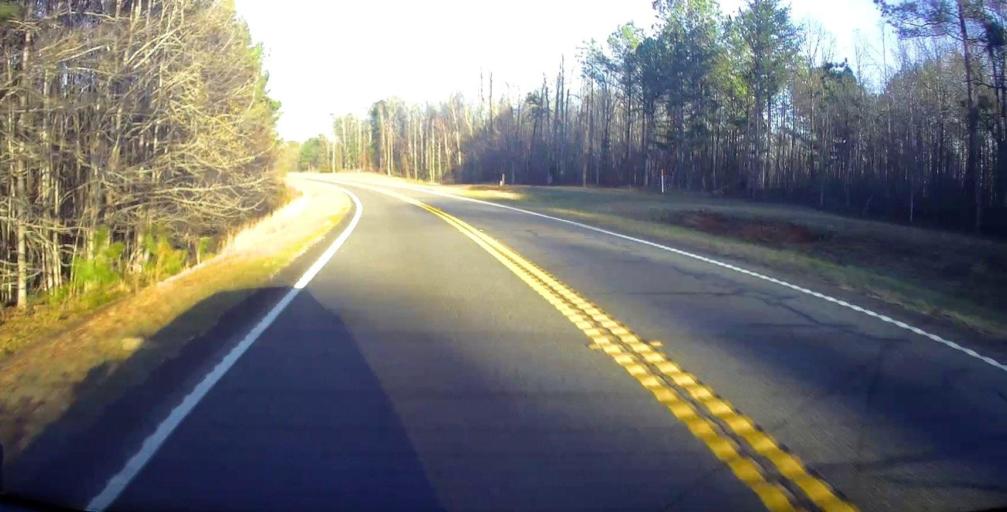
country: US
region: Georgia
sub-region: Talbot County
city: Talbotton
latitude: 32.6582
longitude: -84.6457
